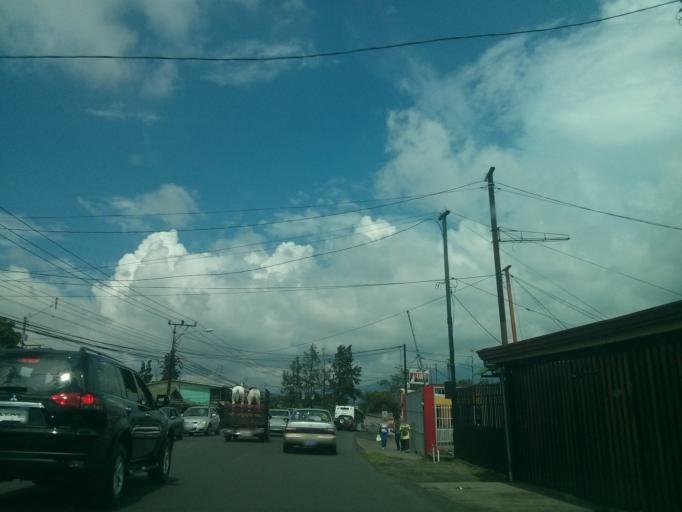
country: CR
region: San Jose
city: San Rafael Arriba
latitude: 9.8802
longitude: -84.0734
